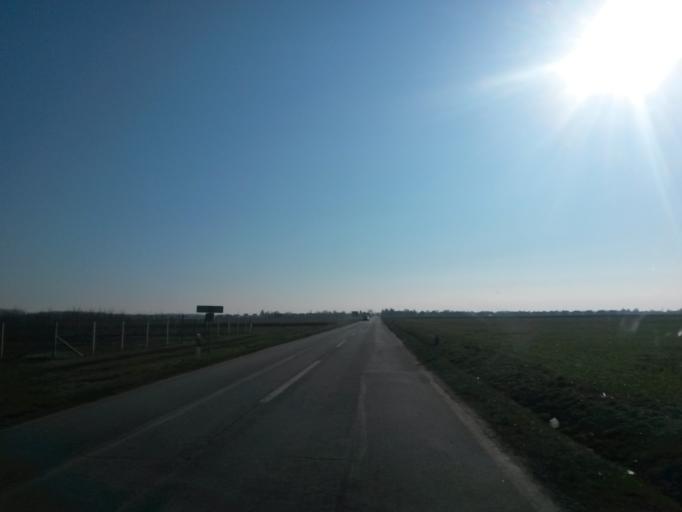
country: HR
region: Osjecko-Baranjska
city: Sarvas
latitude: 45.5329
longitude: 18.8179
